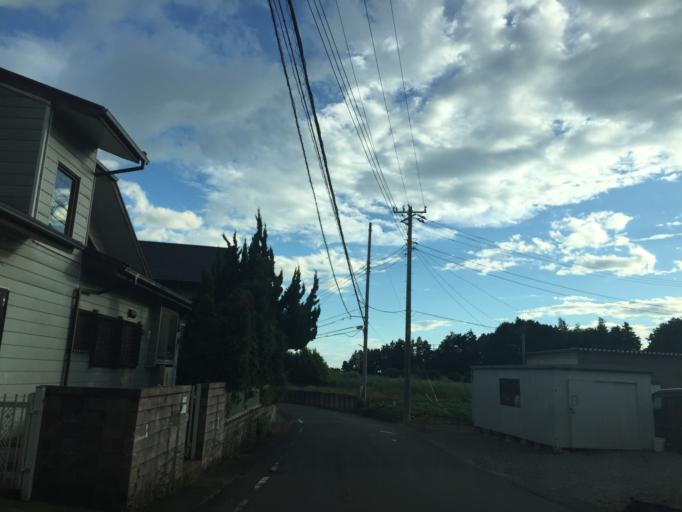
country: JP
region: Shizuoka
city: Mishima
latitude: 35.1572
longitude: 138.9160
